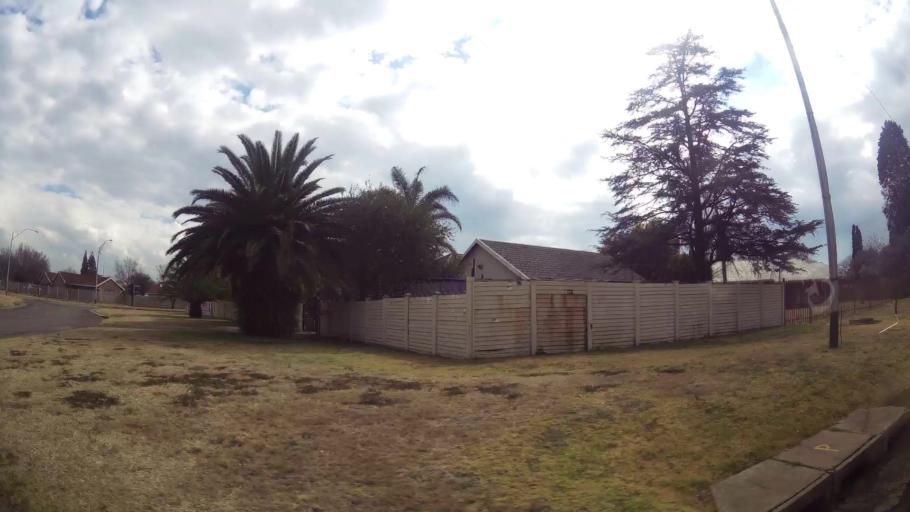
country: ZA
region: Gauteng
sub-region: Sedibeng District Municipality
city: Vereeniging
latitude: -26.6547
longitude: 27.9815
